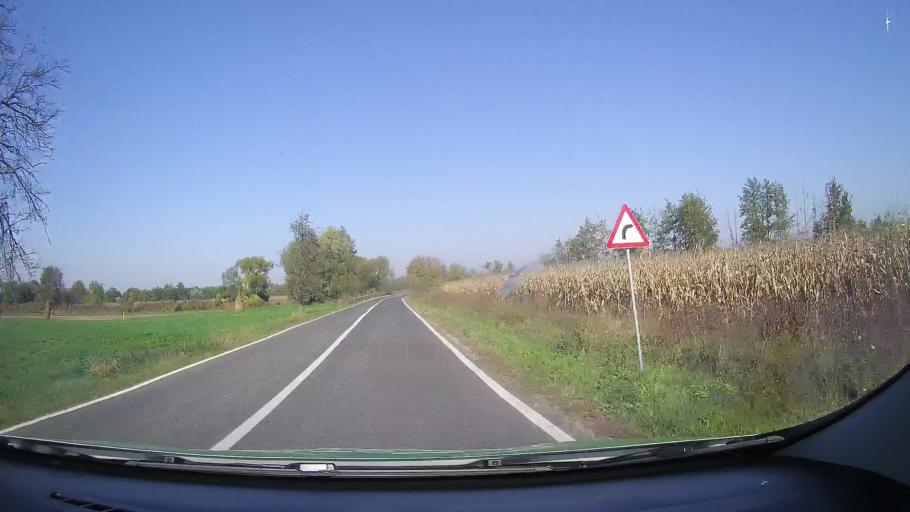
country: RO
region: Timis
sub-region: Comuna Curtea
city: Curtea
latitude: 45.8340
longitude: 22.3105
